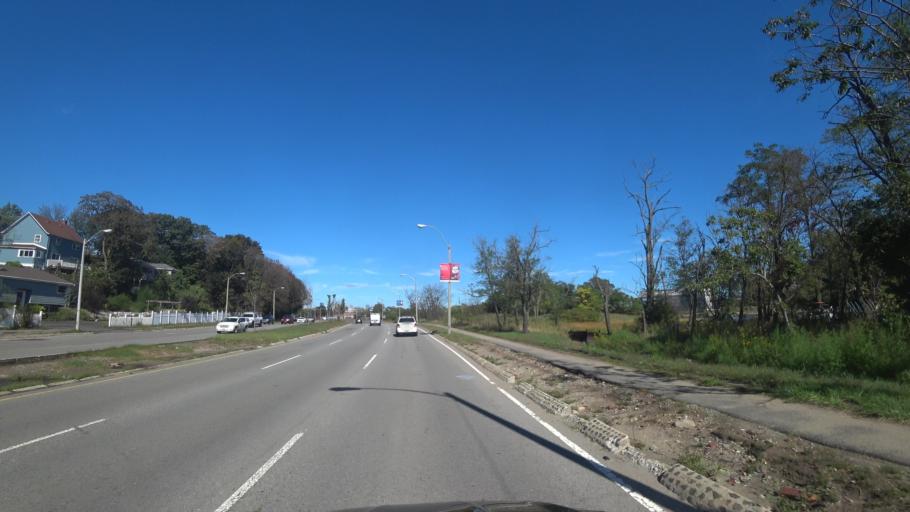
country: US
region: Massachusetts
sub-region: Suffolk County
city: South Boston
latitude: 42.3093
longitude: -71.0453
